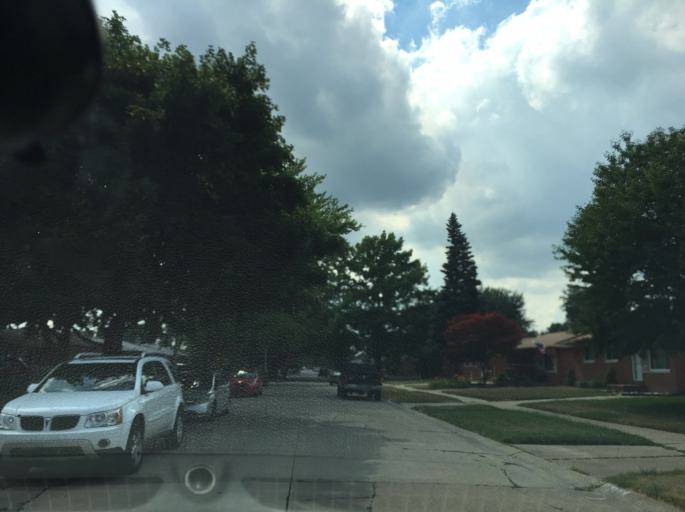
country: US
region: Michigan
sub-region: Macomb County
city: Clinton
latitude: 42.5507
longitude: -82.9121
